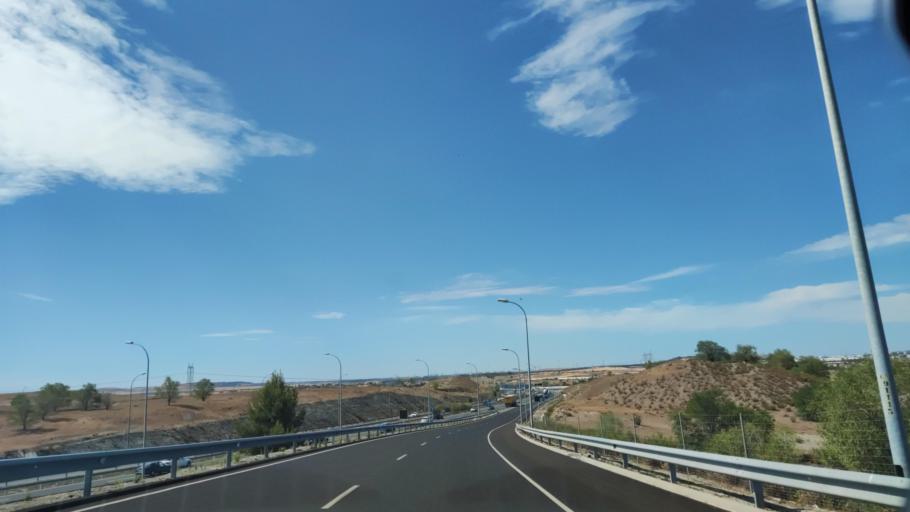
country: ES
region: Madrid
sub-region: Provincia de Madrid
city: Villa de Vallecas
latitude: 40.3338
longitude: -3.6315
